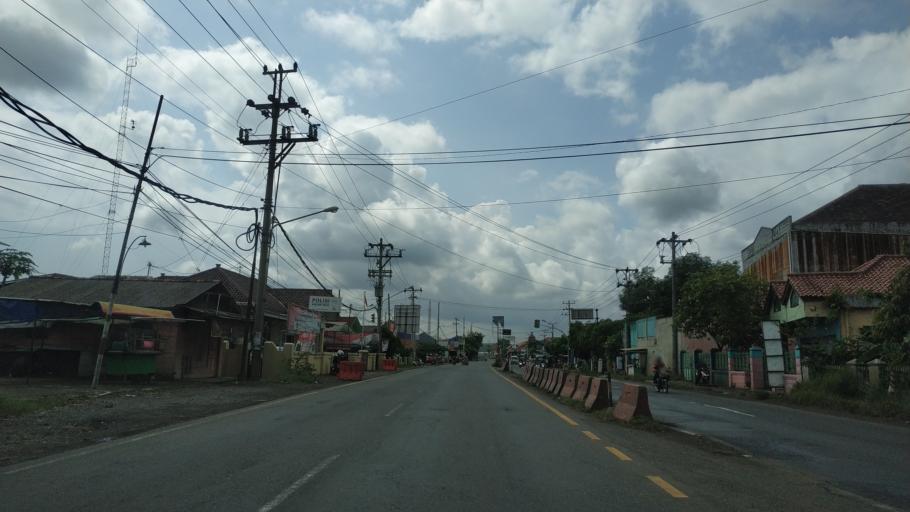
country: ID
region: Central Java
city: Pekalongan
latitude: -6.9515
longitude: 109.8007
